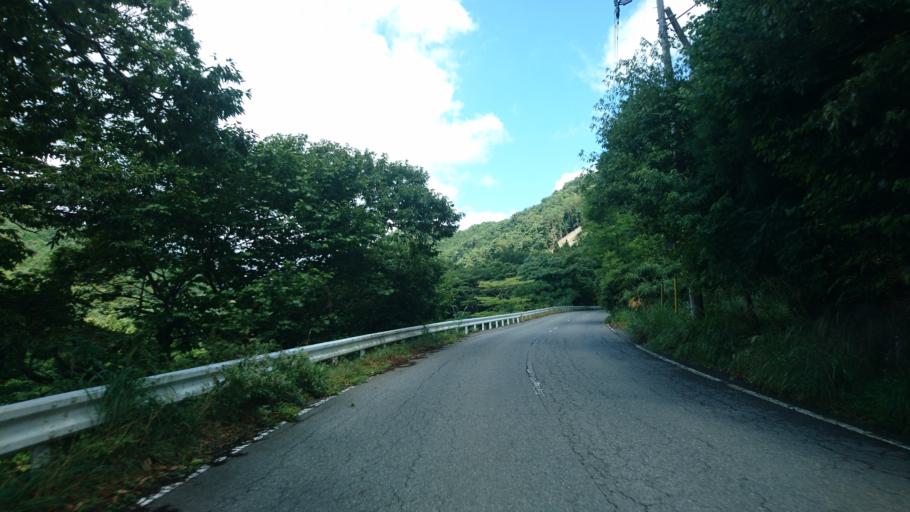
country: JP
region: Gunma
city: Omamacho-omama
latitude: 36.5601
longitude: 139.2538
